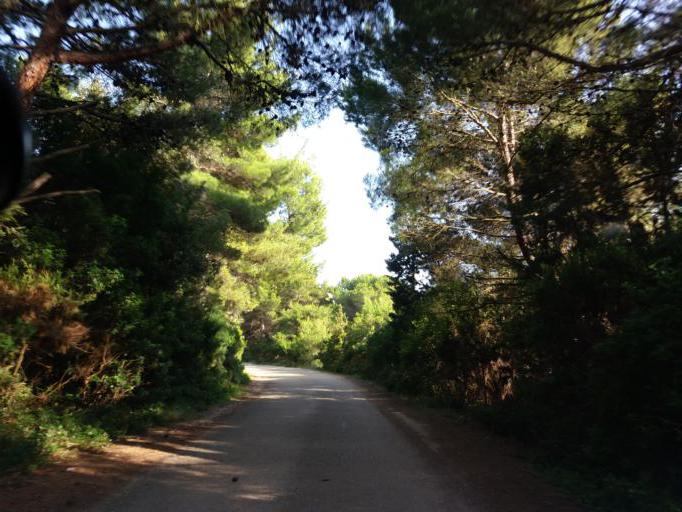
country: HR
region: Zadarska
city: Ugljan
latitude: 44.1517
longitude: 14.8229
